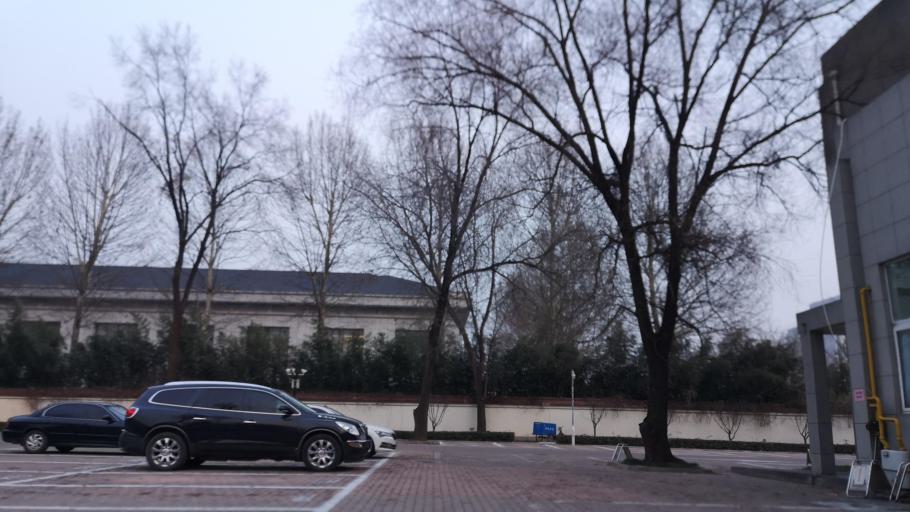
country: CN
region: Henan Sheng
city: Zhongyuanlu
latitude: 35.7787
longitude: 115.0741
